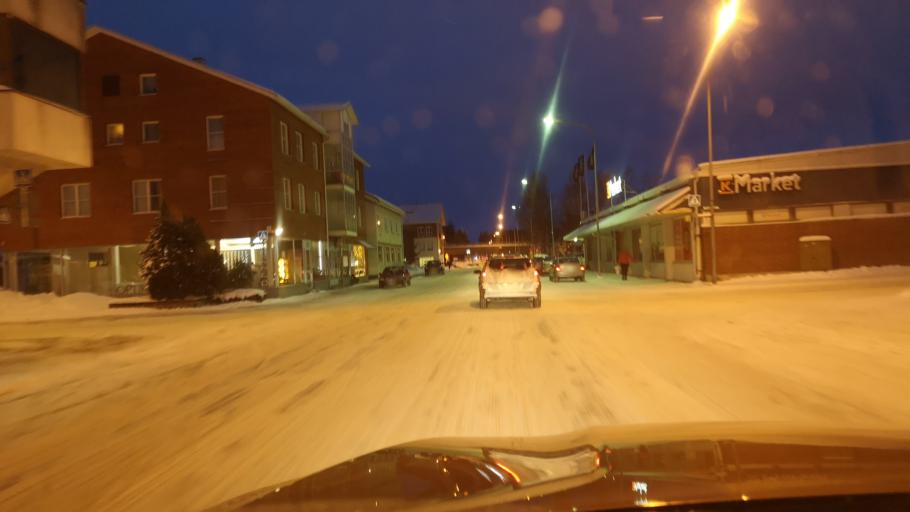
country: FI
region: Varsinais-Suomi
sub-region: Loimaa
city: Loimaa
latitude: 60.8503
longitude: 23.0594
